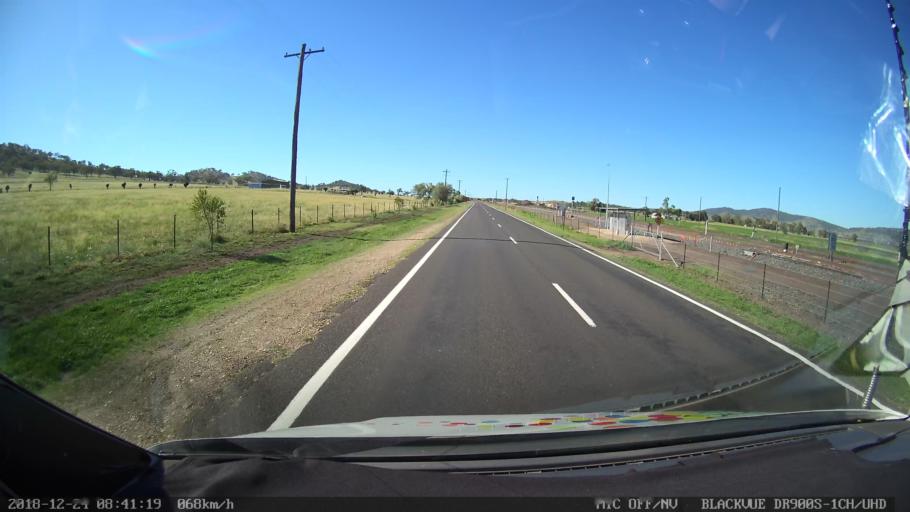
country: AU
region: New South Wales
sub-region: Liverpool Plains
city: Quirindi
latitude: -31.3619
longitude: 150.6452
